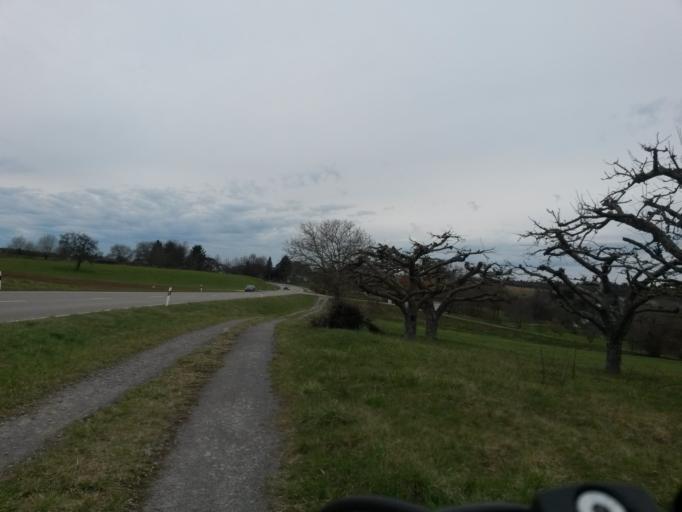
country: DE
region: Baden-Wuerttemberg
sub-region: Karlsruhe Region
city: Neuenburg
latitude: 48.9099
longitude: 8.5339
